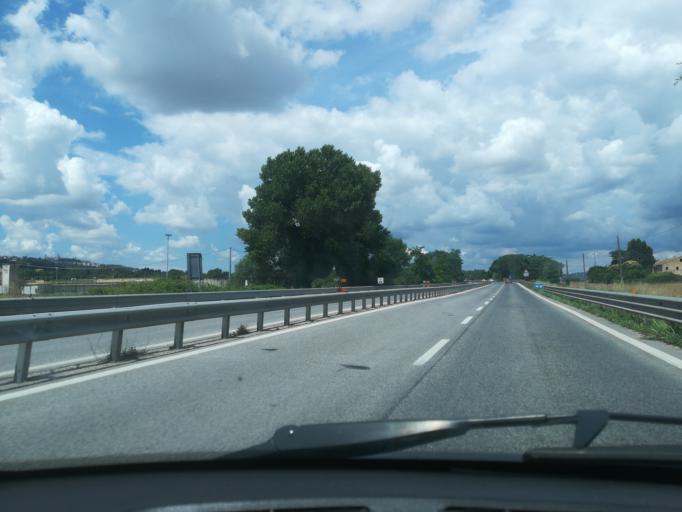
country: IT
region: The Marches
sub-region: Provincia di Macerata
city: Corridonia
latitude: 43.2651
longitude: 13.5477
